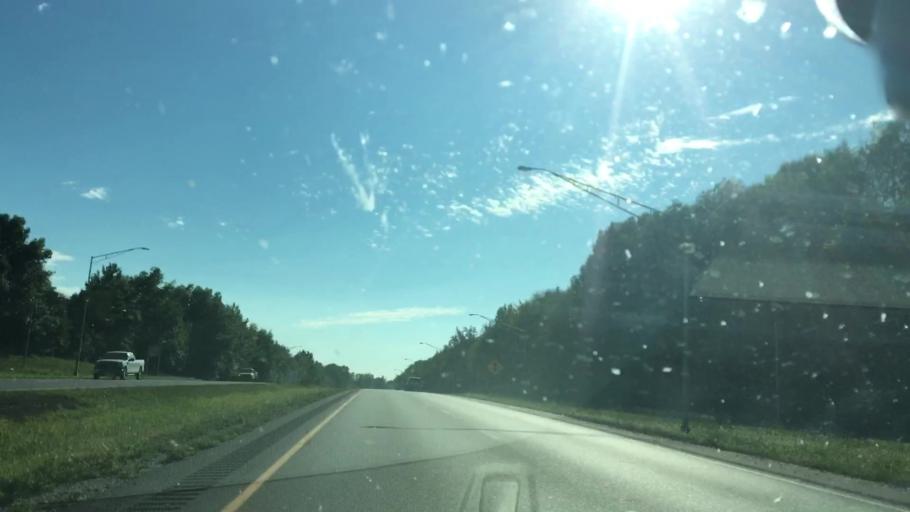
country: US
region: Kentucky
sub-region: Daviess County
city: Owensboro
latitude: 37.7308
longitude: -87.0900
